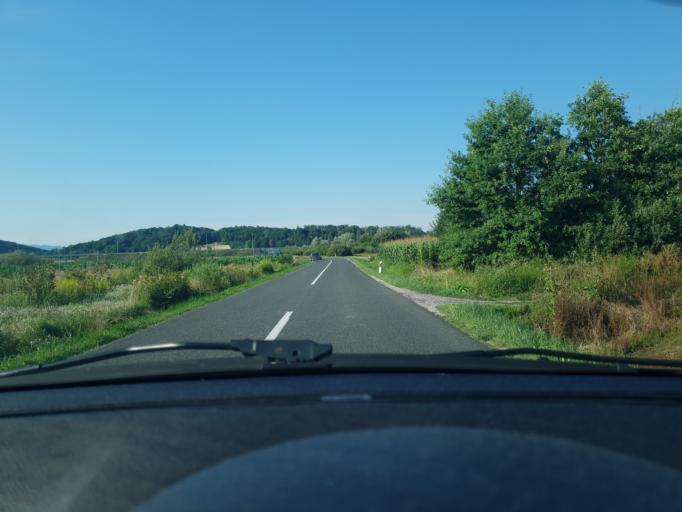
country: HR
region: Krapinsko-Zagorska
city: Oroslavje
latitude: 46.0091
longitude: 15.9314
